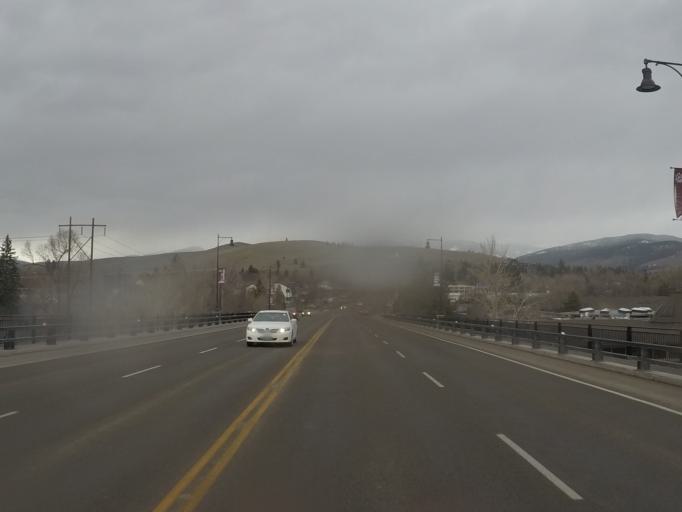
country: US
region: Montana
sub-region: Missoula County
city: Missoula
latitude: 46.8667
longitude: -113.9879
